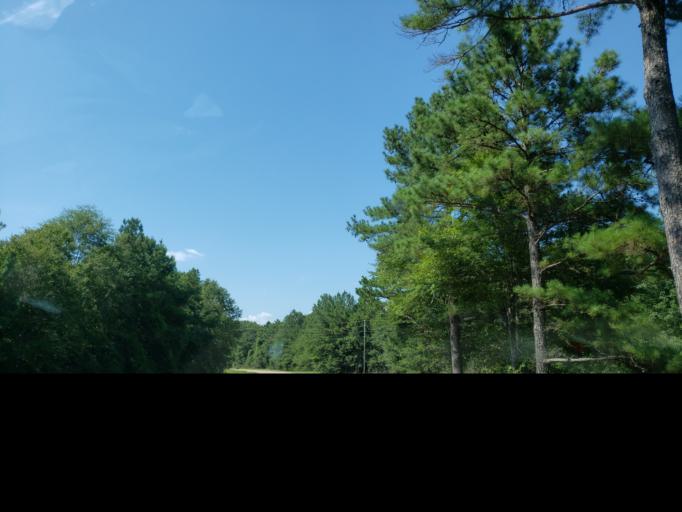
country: US
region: Mississippi
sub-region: Lamar County
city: Sumrall
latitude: 31.4741
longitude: -89.5210
